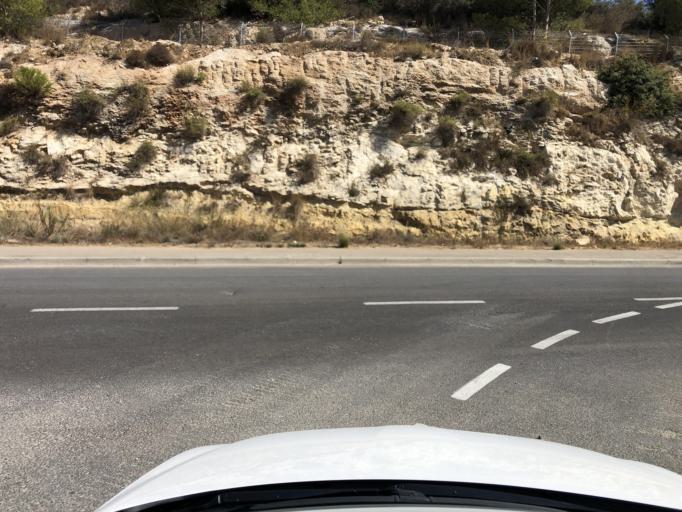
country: PS
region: West Bank
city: An Nabi Ilyas
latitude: 32.1655
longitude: 35.0225
